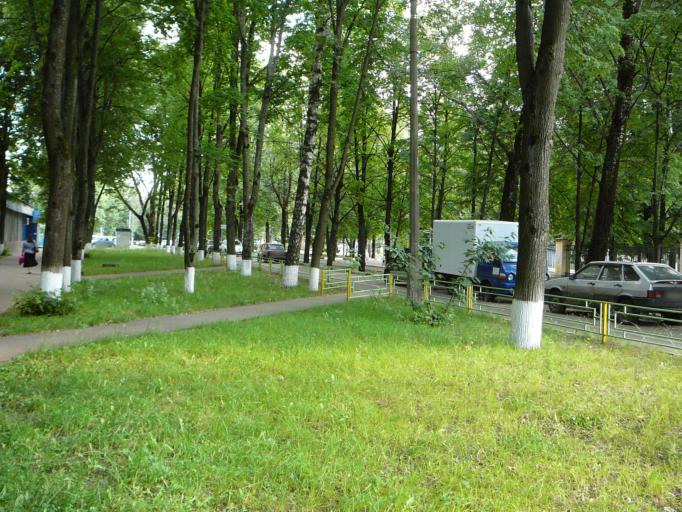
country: RU
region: Moskovskaya
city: Krasnogorsk
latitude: 55.8287
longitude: 37.3293
